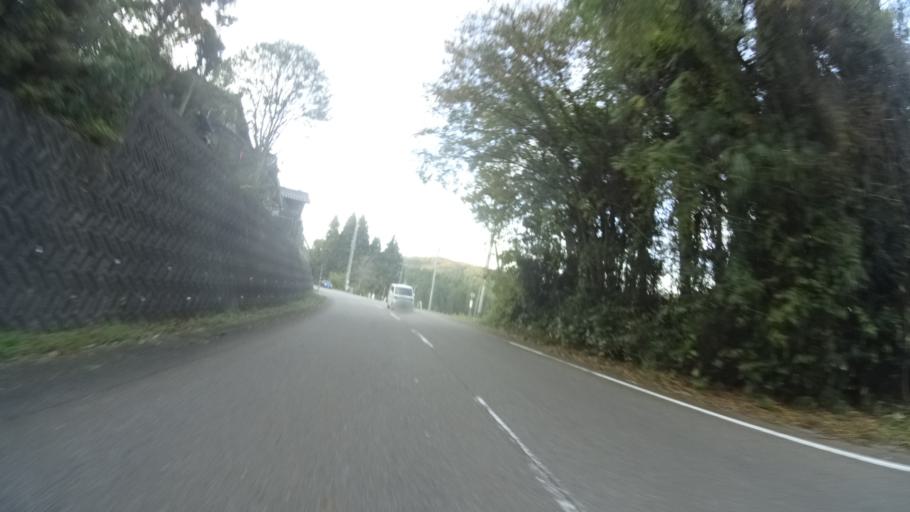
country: JP
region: Ishikawa
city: Nanao
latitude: 37.1963
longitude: 136.7139
